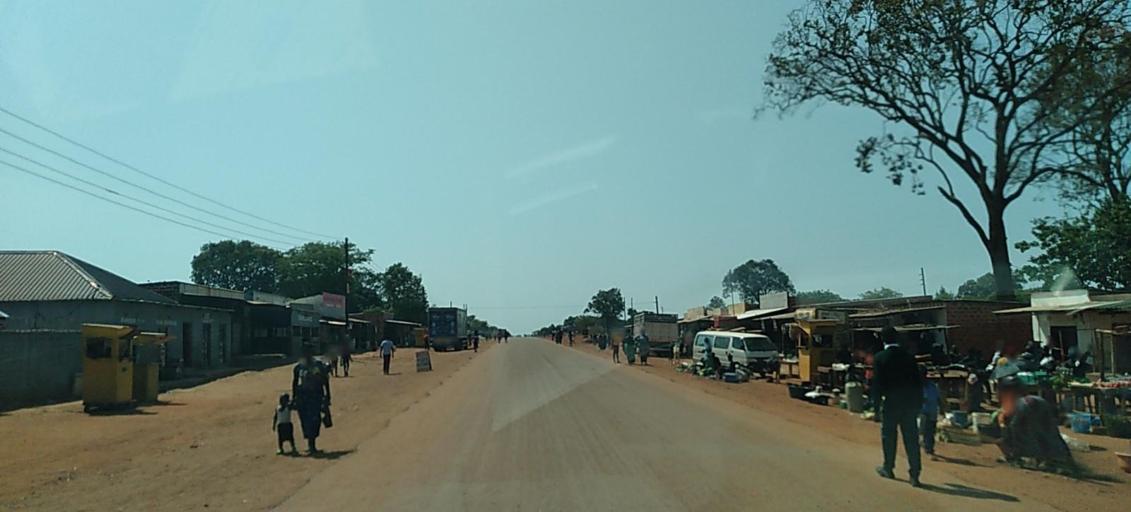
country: ZM
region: North-Western
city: Solwezi
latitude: -12.1096
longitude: 25.4983
